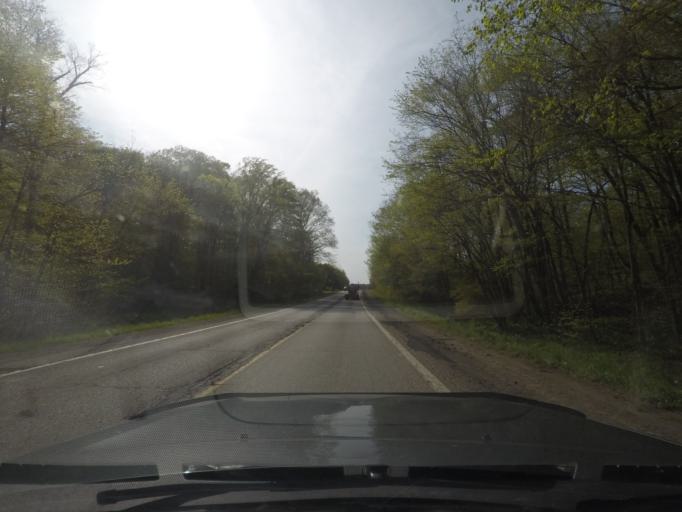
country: US
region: Michigan
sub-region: Berrien County
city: Buchanan
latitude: 41.7942
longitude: -86.4480
